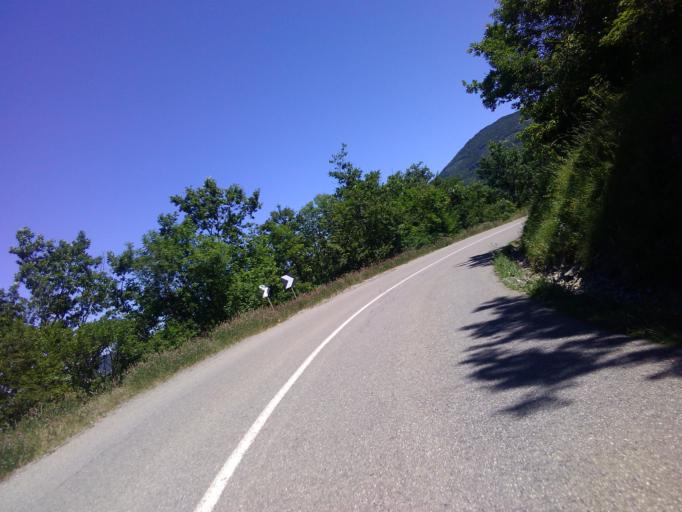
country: IT
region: Emilia-Romagna
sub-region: Provincia di Parma
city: Berceto
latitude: 44.5313
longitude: 10.0219
